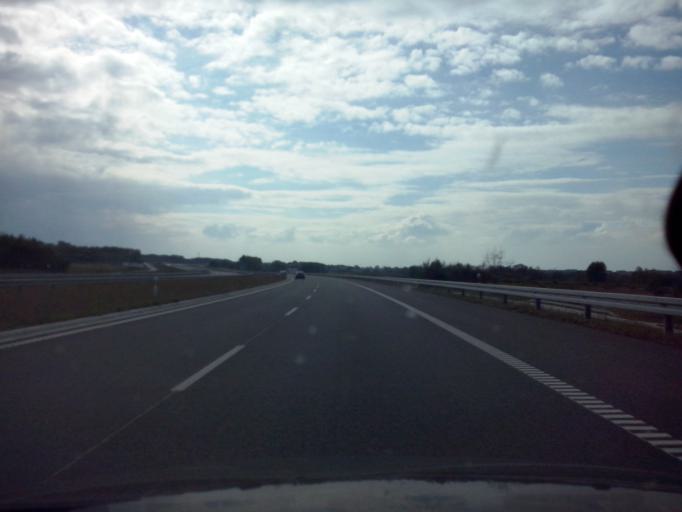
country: PL
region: Lesser Poland Voivodeship
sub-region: Powiat tarnowski
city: Lisia Gora
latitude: 50.0627
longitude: 21.0465
